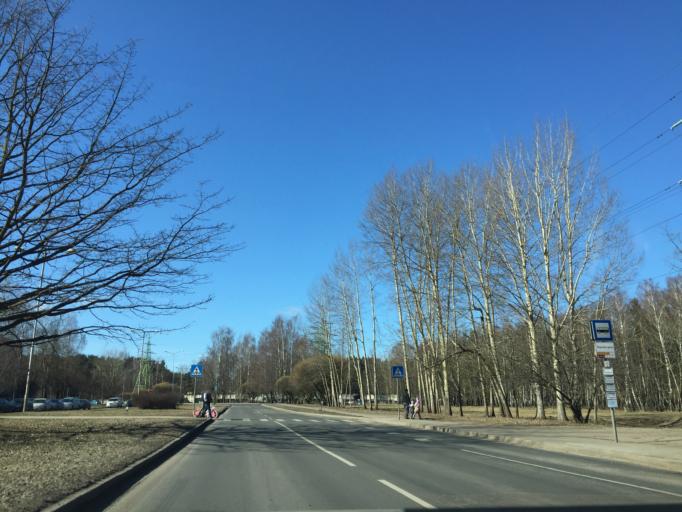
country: LV
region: Marupe
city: Marupe
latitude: 56.9688
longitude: 24.0177
